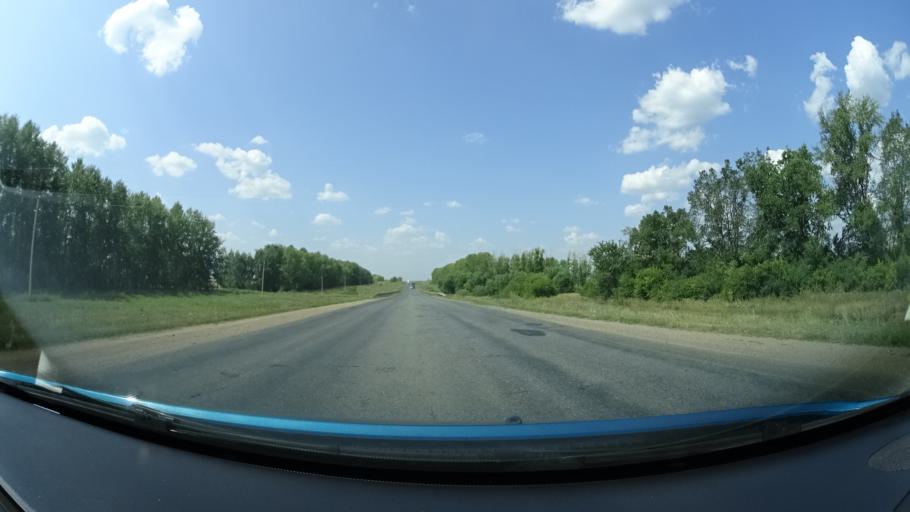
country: RU
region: Bashkortostan
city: Buzdyak
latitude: 54.6626
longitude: 54.7093
